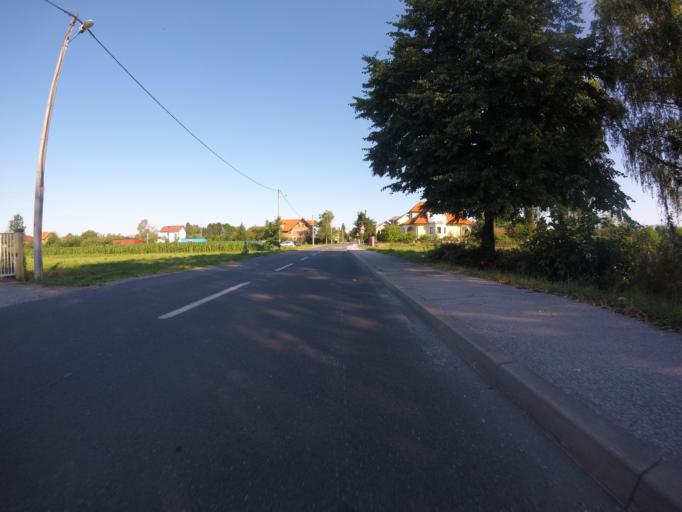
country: HR
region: Grad Zagreb
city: Zadvorsko
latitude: 45.7290
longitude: 15.9048
